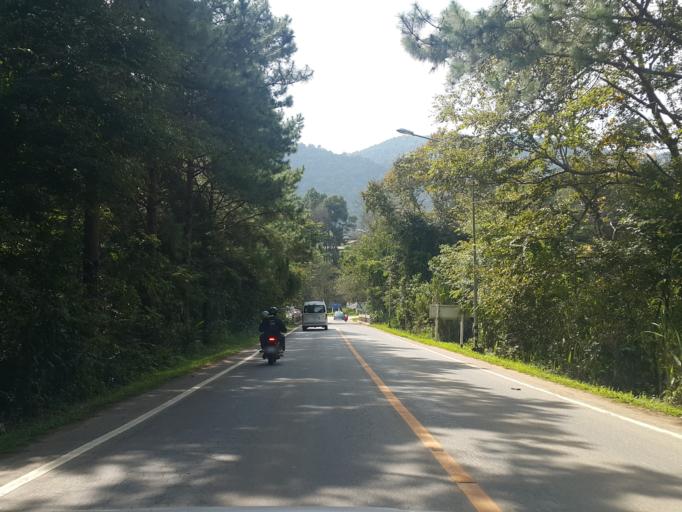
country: TH
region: Chiang Mai
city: Mae Chaem
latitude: 18.5387
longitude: 98.5264
